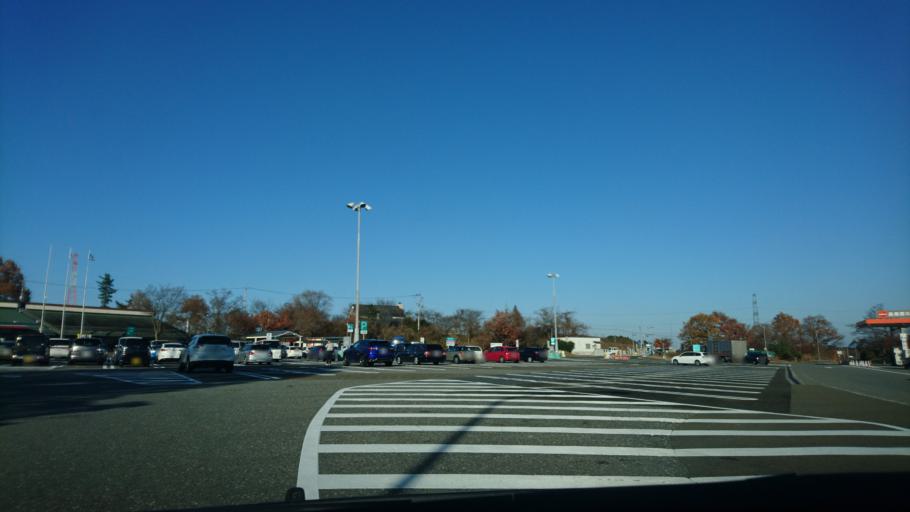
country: JP
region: Miyagi
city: Furukawa
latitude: 38.6370
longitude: 140.9592
